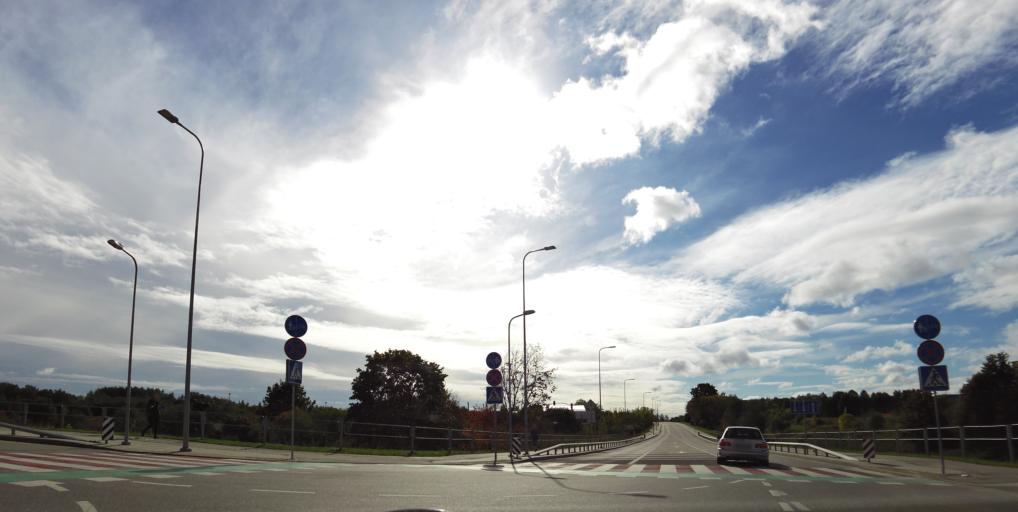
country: LT
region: Vilnius County
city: Naujamiestis
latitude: 54.6502
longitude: 25.2765
